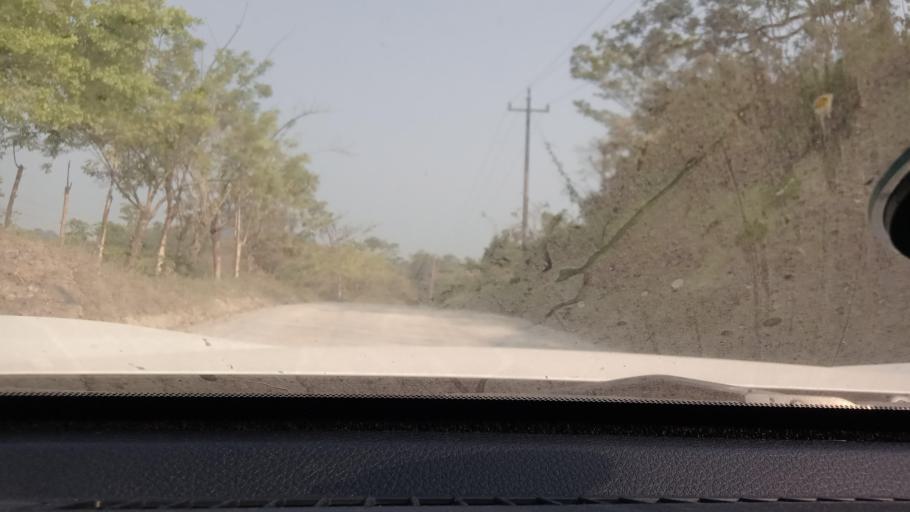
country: MX
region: Tabasco
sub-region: Huimanguillo
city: Francisco Rueda
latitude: 17.6159
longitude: -93.9400
